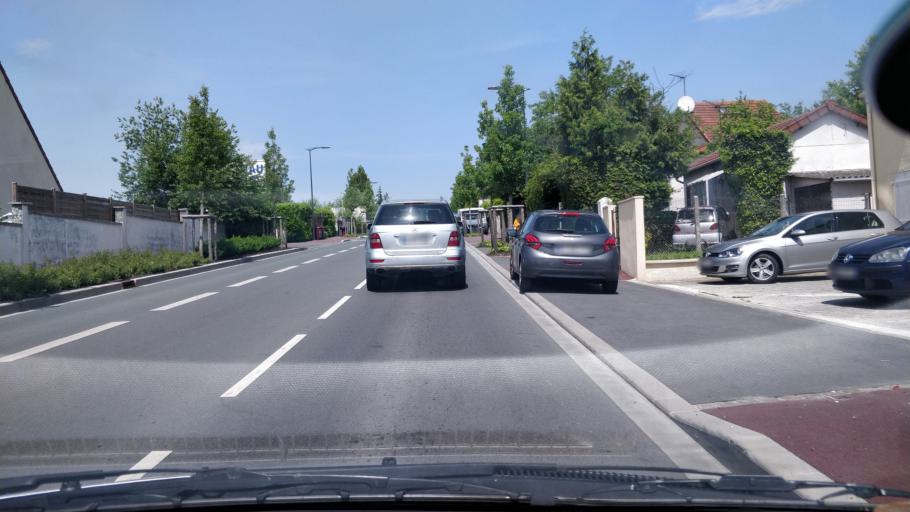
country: FR
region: Ile-de-France
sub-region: Departement de Seine-Saint-Denis
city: Montfermeil
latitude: 48.8921
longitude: 2.5798
